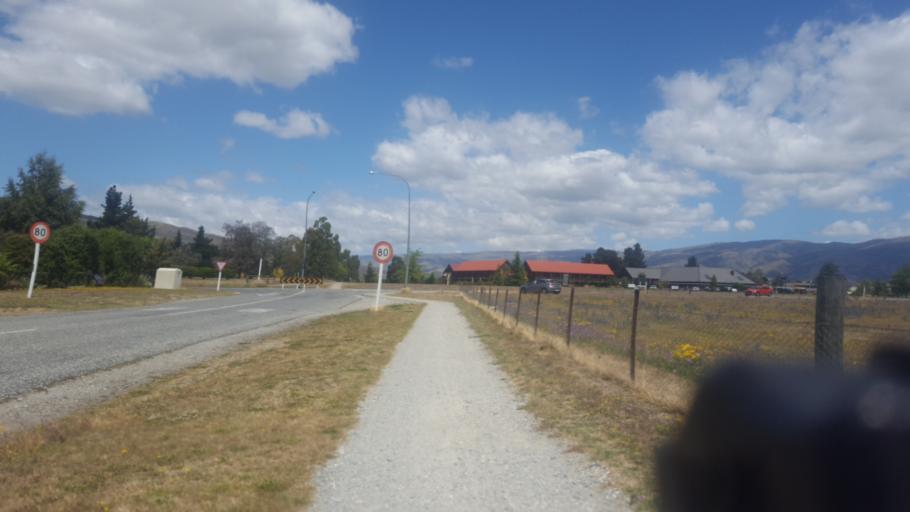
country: NZ
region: Otago
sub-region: Queenstown-Lakes District
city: Wanaka
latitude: -45.0338
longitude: 169.2024
